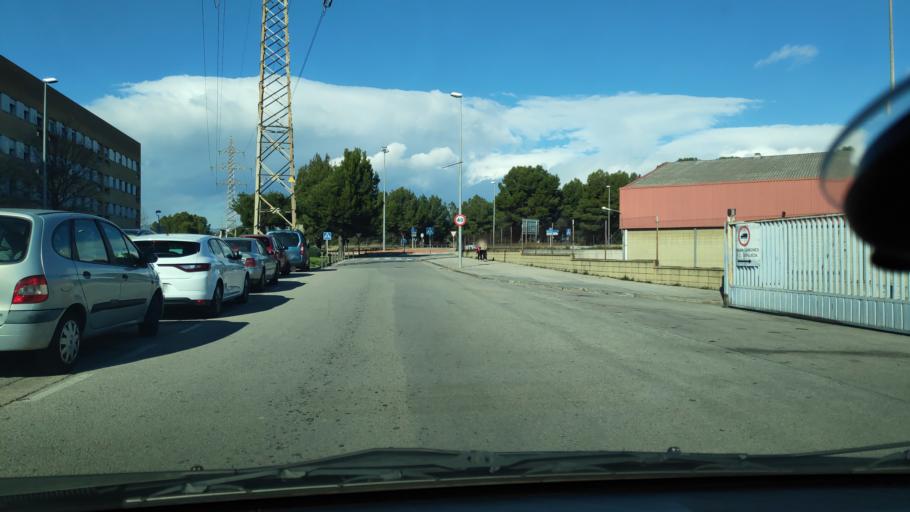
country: ES
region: Catalonia
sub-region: Provincia de Barcelona
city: Sant Quirze del Valles
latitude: 41.5417
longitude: 2.0705
